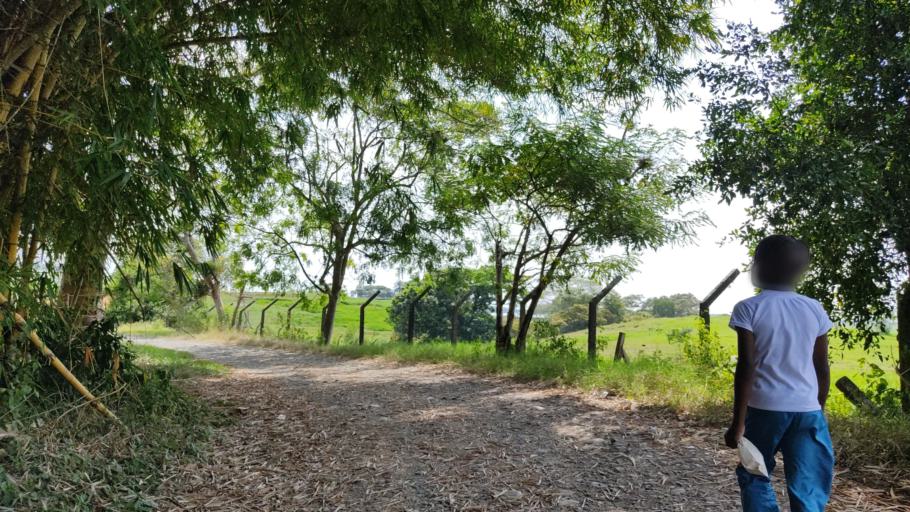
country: CO
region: Cauca
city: Buenos Aires
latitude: 3.1347
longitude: -76.5916
